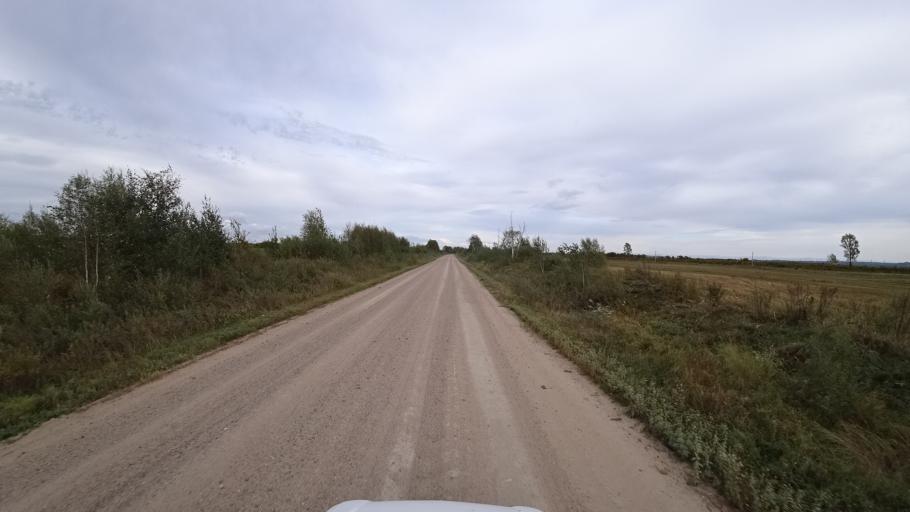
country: RU
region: Amur
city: Arkhara
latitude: 49.3750
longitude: 130.1614
